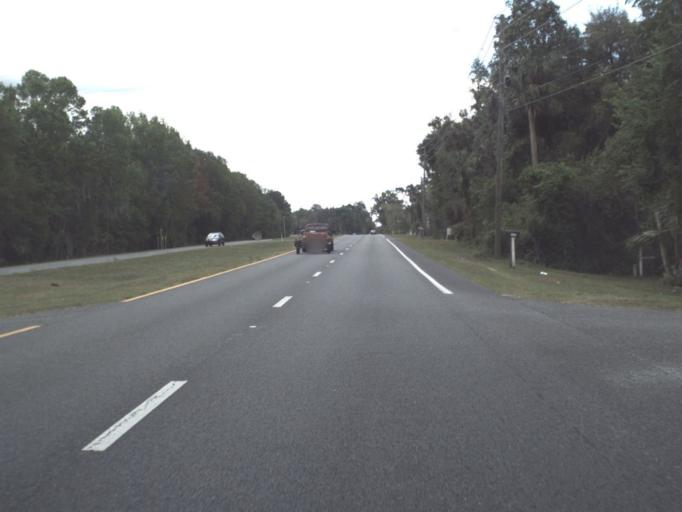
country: US
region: Florida
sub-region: Marion County
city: Citra
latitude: 29.4615
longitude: -82.2224
